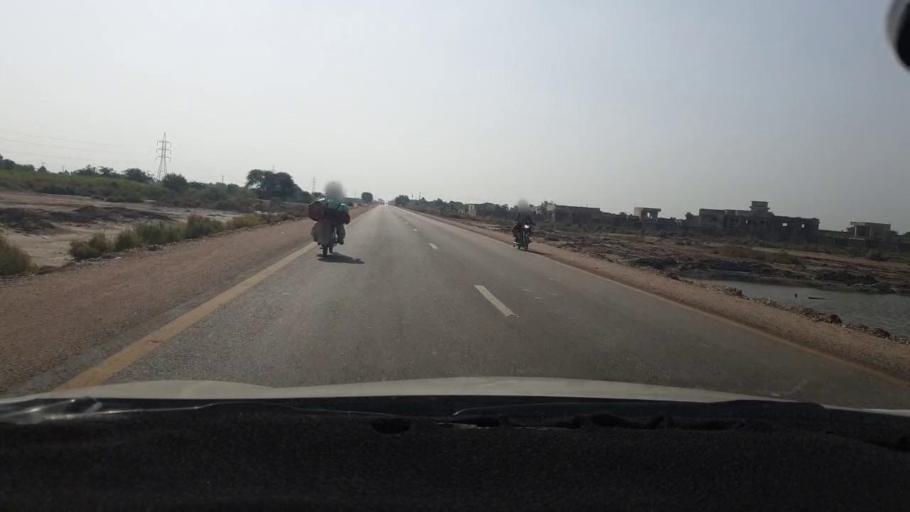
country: PK
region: Sindh
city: Jhol
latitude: 25.9192
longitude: 69.0057
